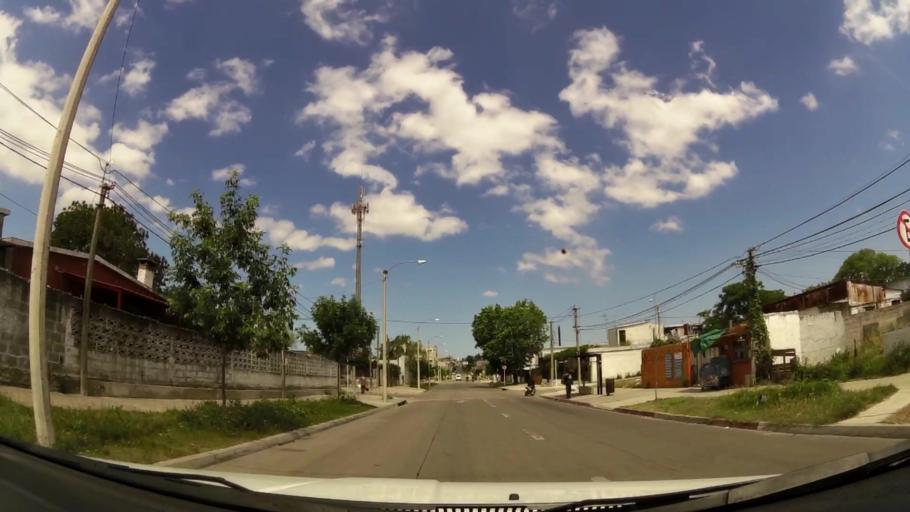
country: UY
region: Montevideo
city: Montevideo
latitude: -34.8454
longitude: -56.2388
